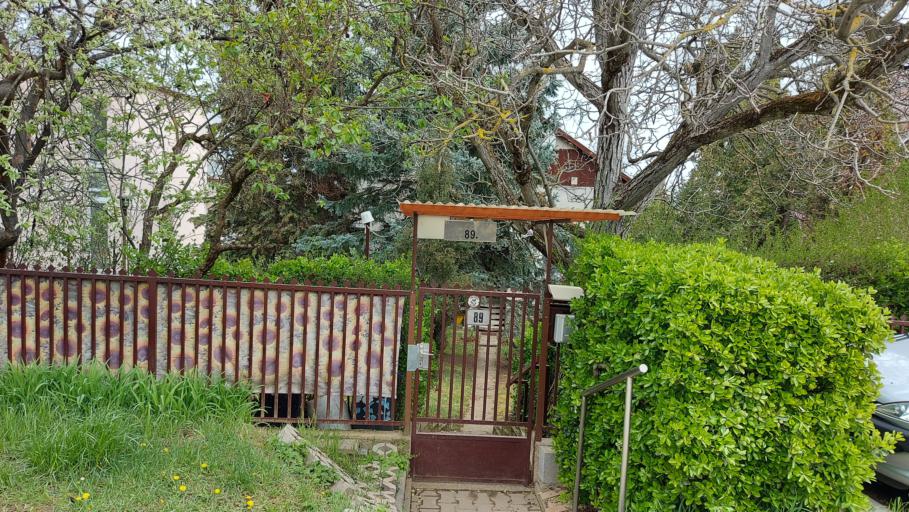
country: HU
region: Pest
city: Budaors
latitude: 47.4367
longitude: 18.9692
